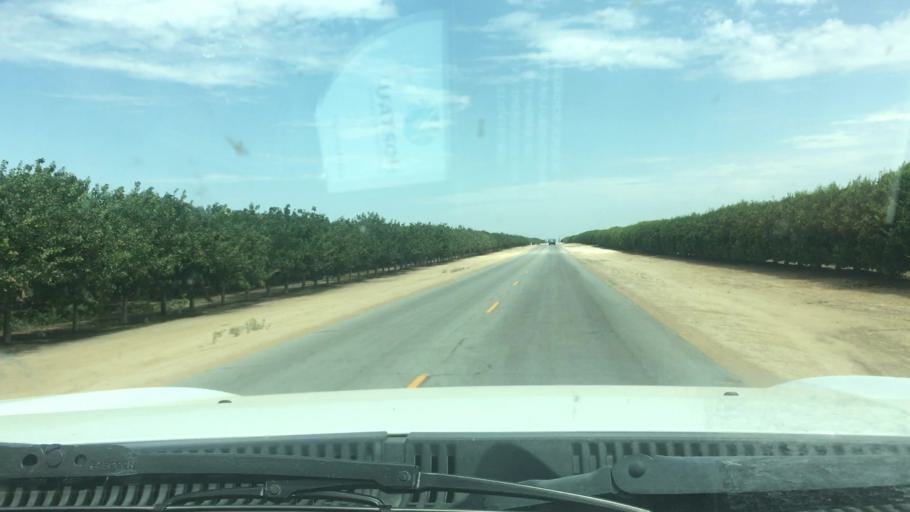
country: US
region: California
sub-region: Kern County
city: McFarland
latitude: 35.5757
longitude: -119.1511
